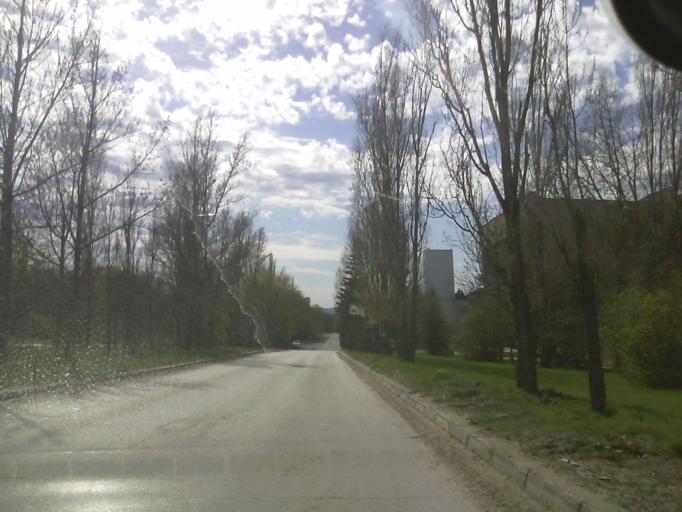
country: RU
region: Saratov
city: Sokolovyy
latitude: 51.5937
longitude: 45.9144
